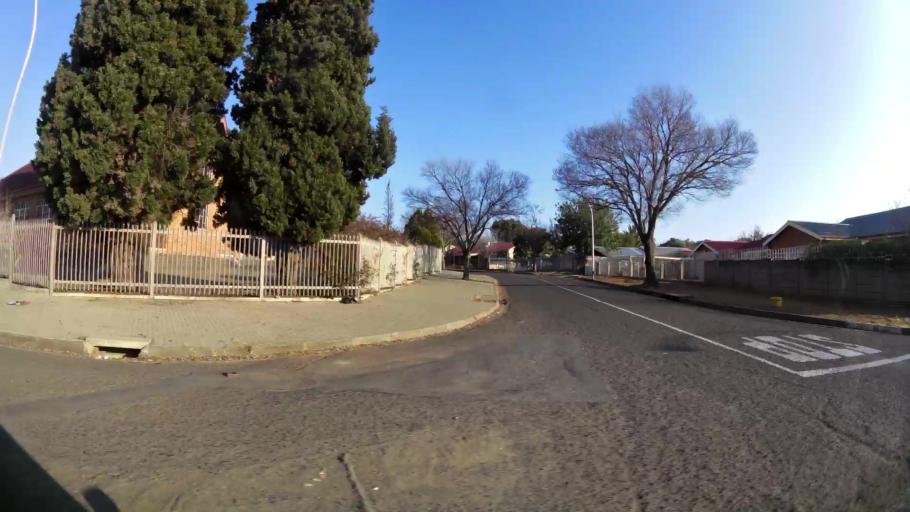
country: ZA
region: Orange Free State
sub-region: Mangaung Metropolitan Municipality
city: Bloemfontein
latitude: -29.1518
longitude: 26.1998
